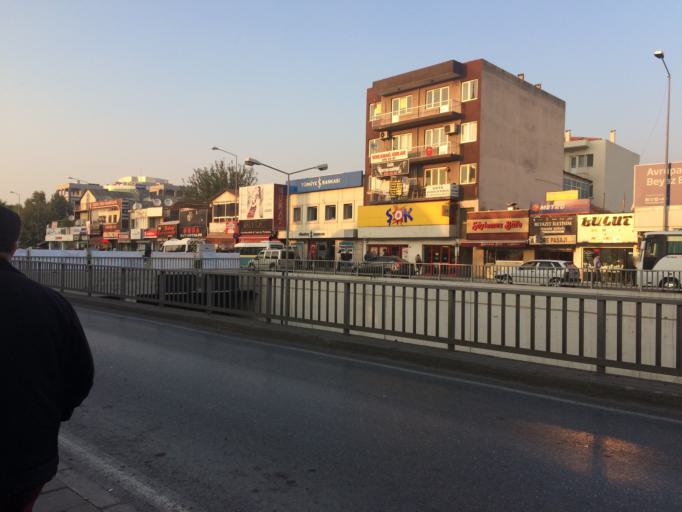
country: TR
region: Izmir
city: Karsiyaka
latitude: 38.4931
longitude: 27.0632
